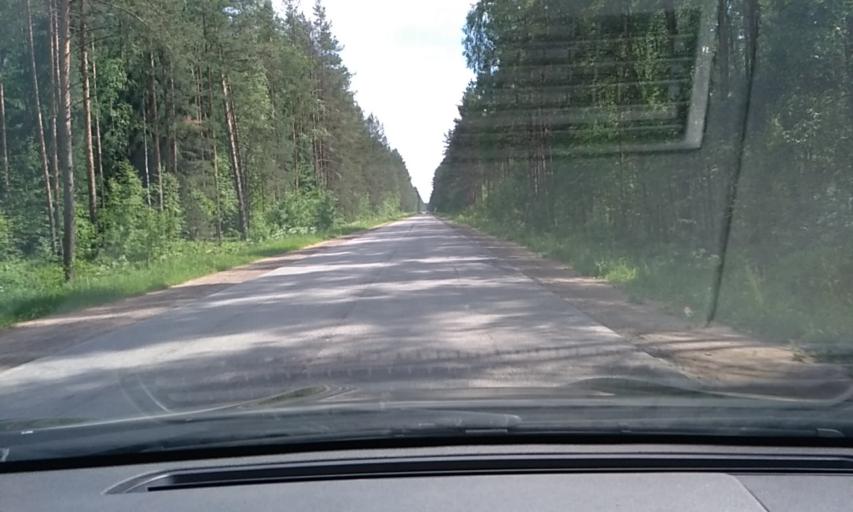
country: RU
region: Leningrad
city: Imeni Sverdlova
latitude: 59.8412
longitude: 30.6923
